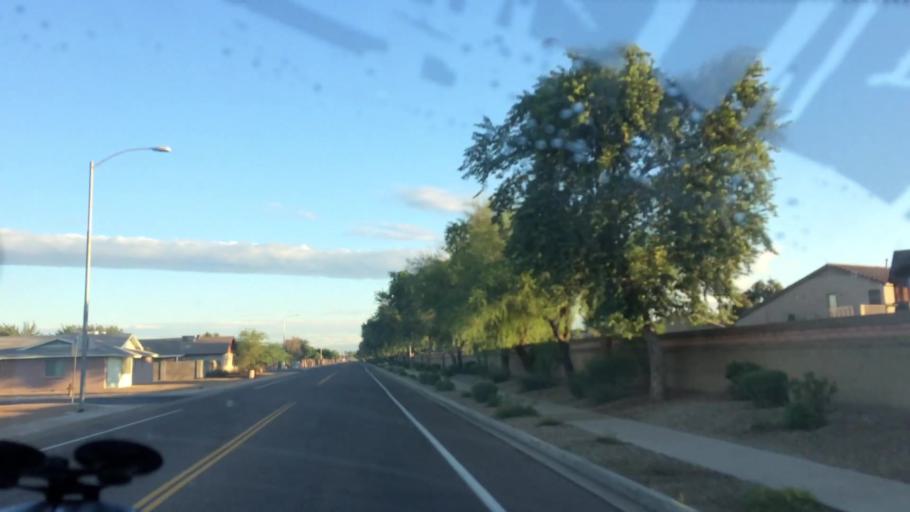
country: US
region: Arizona
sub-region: Maricopa County
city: Sun City
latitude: 33.5719
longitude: -112.2638
